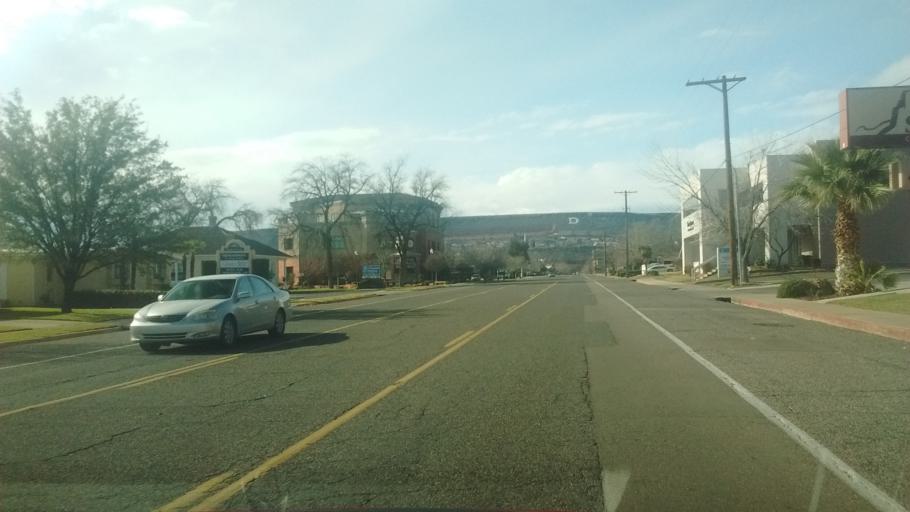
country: US
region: Utah
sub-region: Washington County
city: Saint George
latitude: 37.1082
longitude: -113.5758
